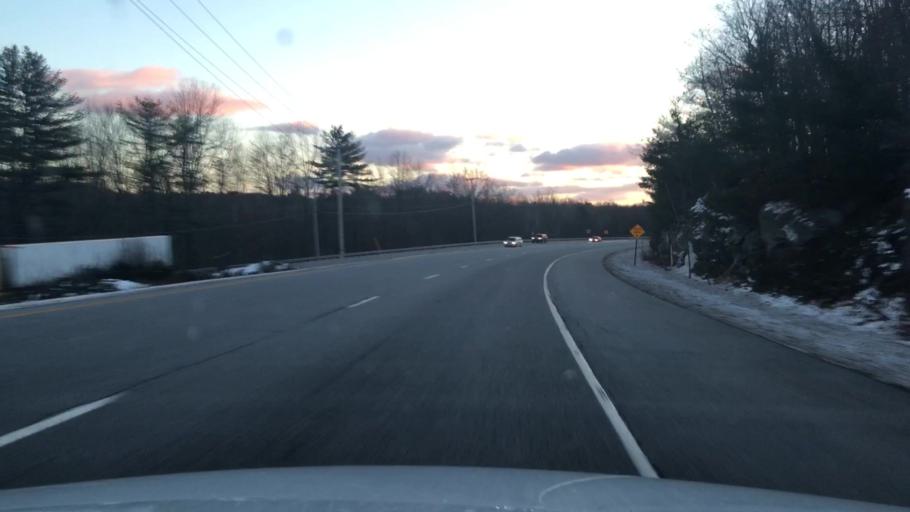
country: US
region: Maine
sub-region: Androscoggin County
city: Auburn
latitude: 44.0490
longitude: -70.2561
